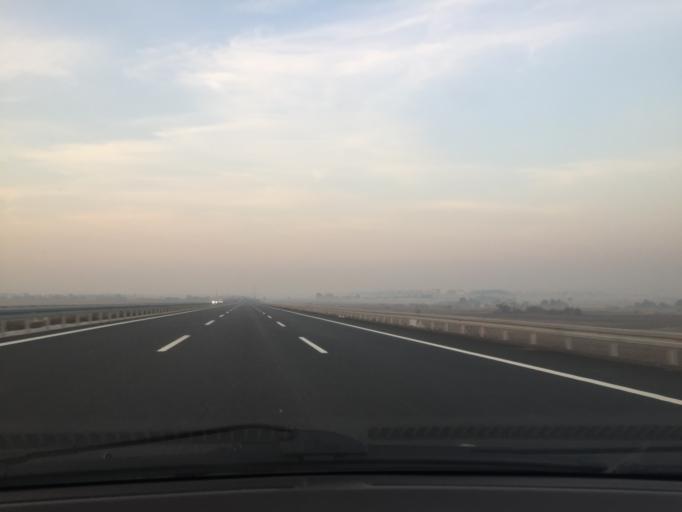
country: TR
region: Bursa
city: Karacabey
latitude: 40.2324
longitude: 28.4167
